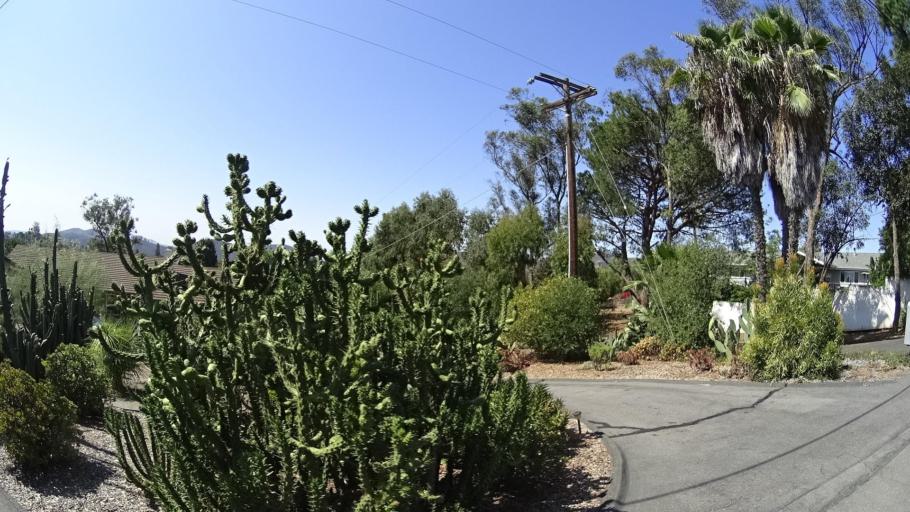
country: US
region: California
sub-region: San Diego County
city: Escondido
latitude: 33.0800
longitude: -117.0975
